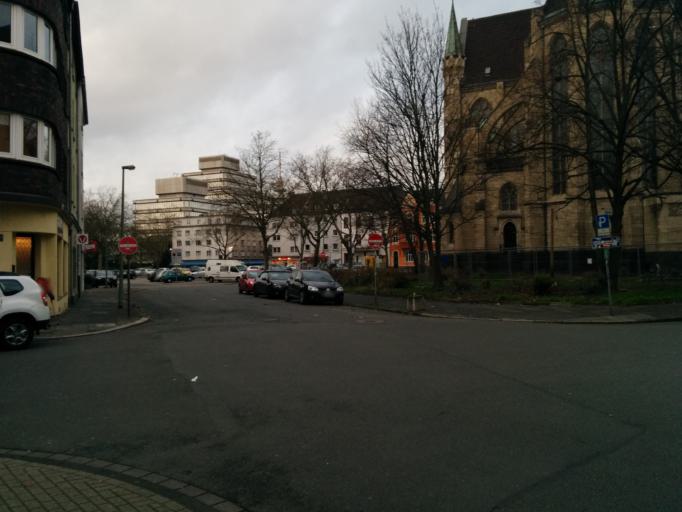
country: DE
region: North Rhine-Westphalia
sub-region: Regierungsbezirk Dusseldorf
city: Duisburg
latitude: 51.4296
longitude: 6.7828
